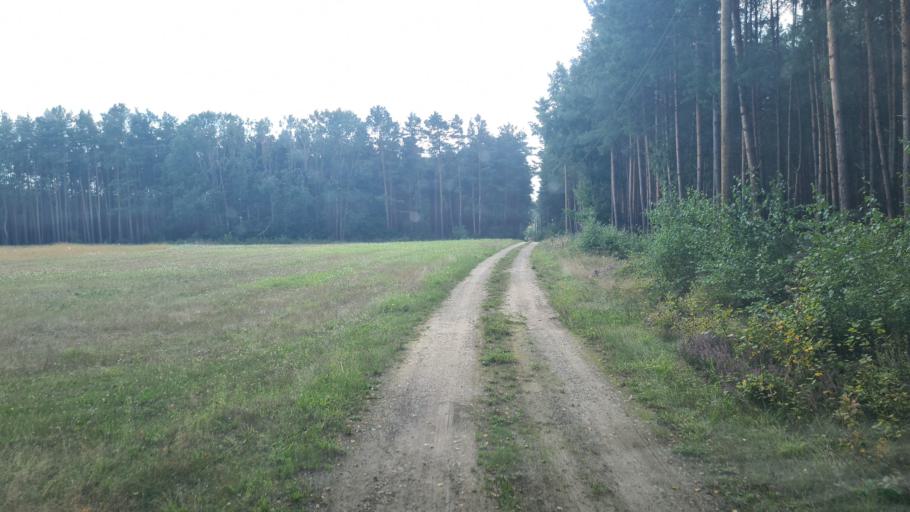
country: DE
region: Brandenburg
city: Schonewalde
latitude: 51.7466
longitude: 13.5980
